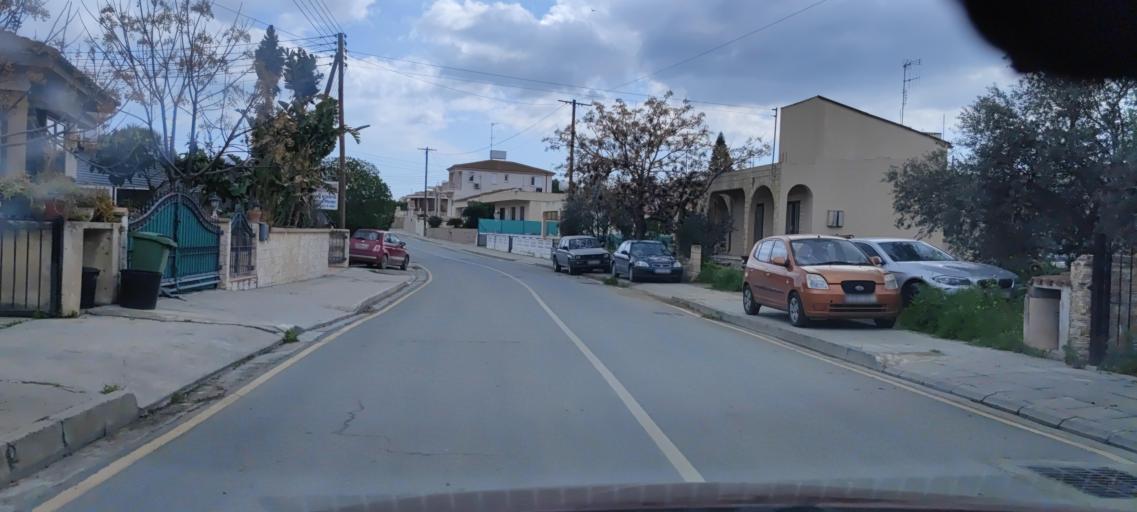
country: CY
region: Larnaka
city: Kornos
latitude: 34.9161
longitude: 33.4016
